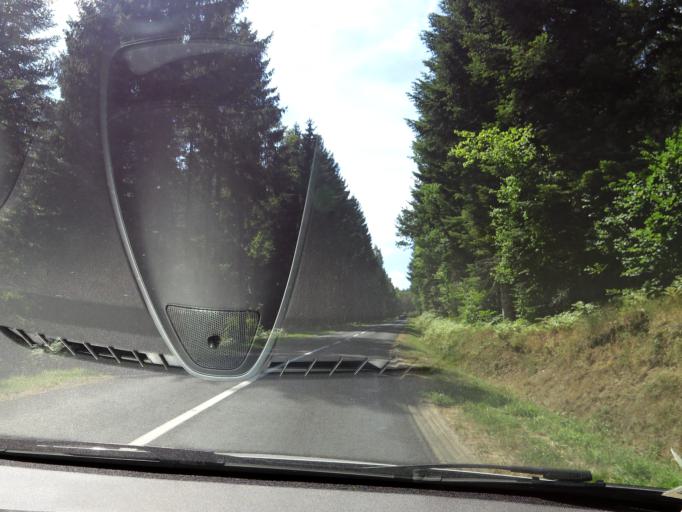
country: FR
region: Auvergne
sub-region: Departement du Puy-de-Dome
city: Orcines
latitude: 45.7674
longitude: 2.9855
